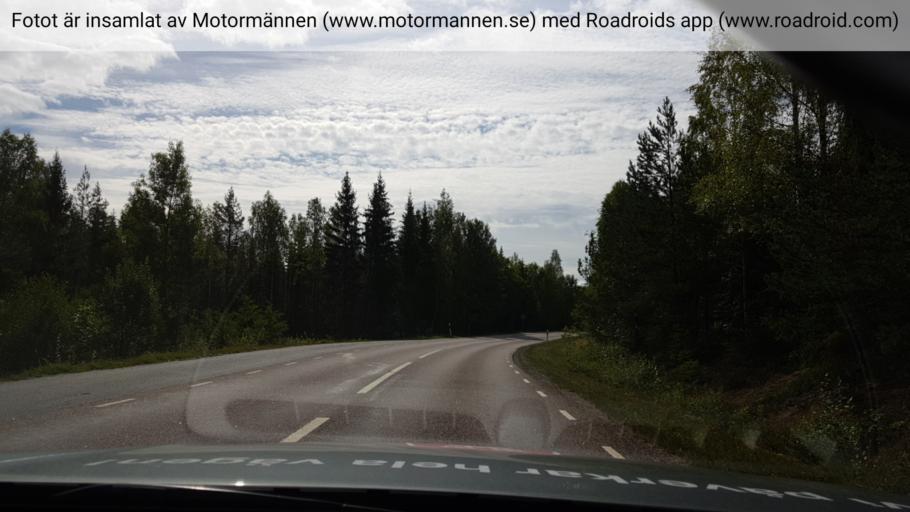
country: SE
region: Uppsala
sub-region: Heby Kommun
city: OEstervala
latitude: 60.0223
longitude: 17.2808
